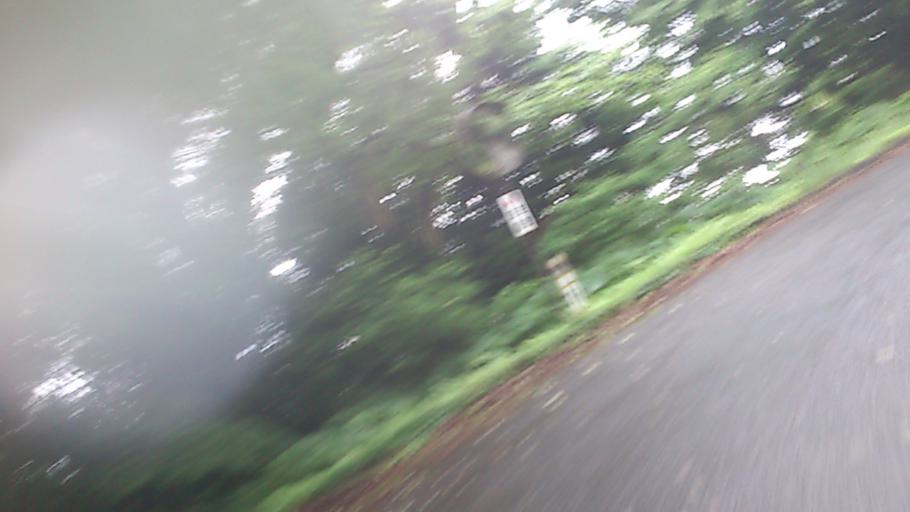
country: JP
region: Akita
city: Noshiromachi
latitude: 40.5571
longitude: 139.9621
